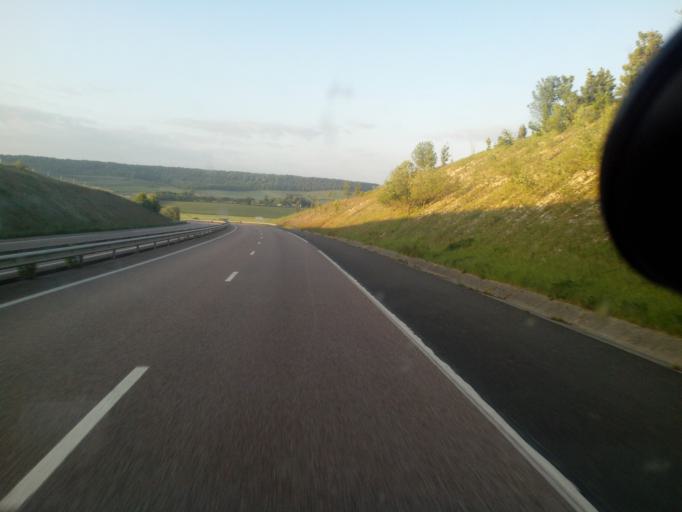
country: FR
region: Haute-Normandie
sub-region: Departement de la Seine-Maritime
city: Blangy-sur-Bresle
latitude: 49.9133
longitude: 1.6291
